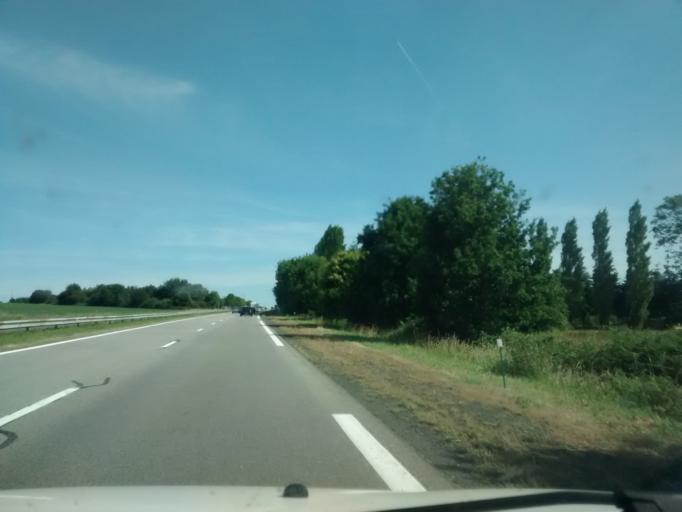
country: FR
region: Brittany
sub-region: Departement d'Ille-et-Vilaine
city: Quedillac
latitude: 48.2468
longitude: -2.1331
